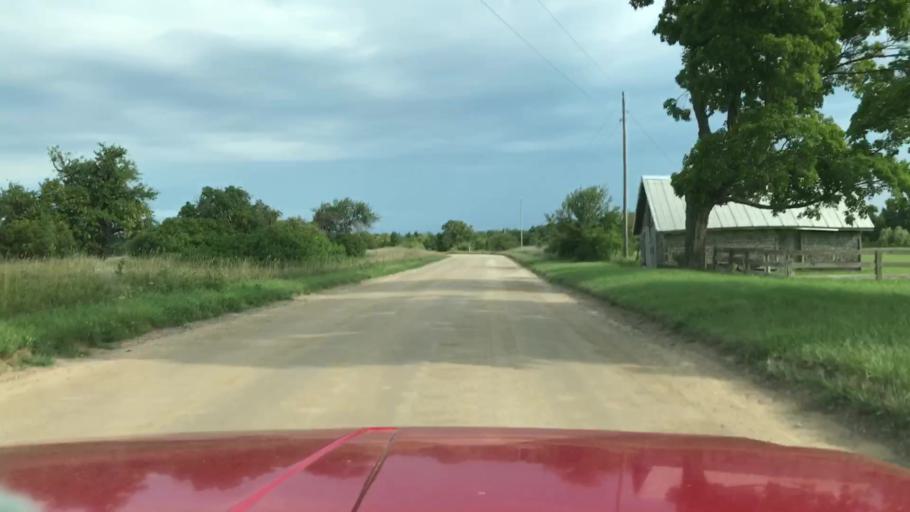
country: US
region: Michigan
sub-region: Charlevoix County
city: Charlevoix
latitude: 45.7260
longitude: -85.5158
